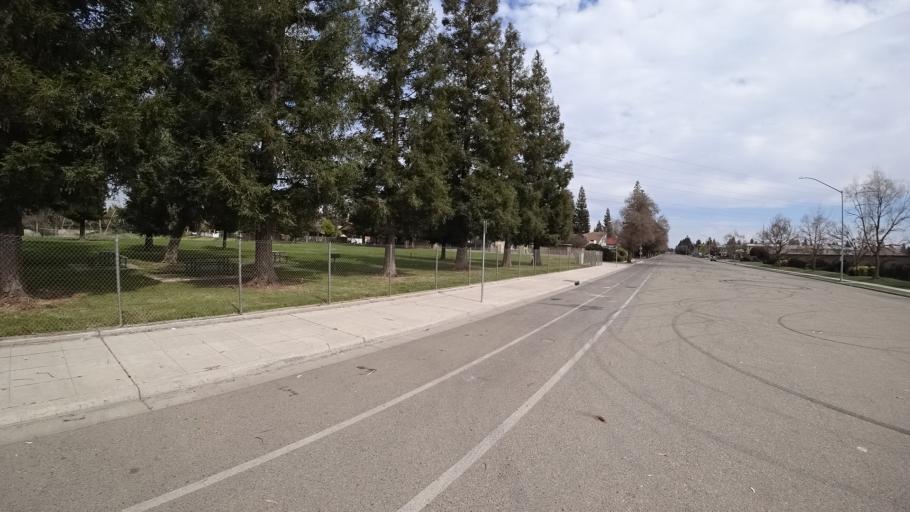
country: US
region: California
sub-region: Fresno County
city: Biola
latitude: 36.8407
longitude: -119.9063
